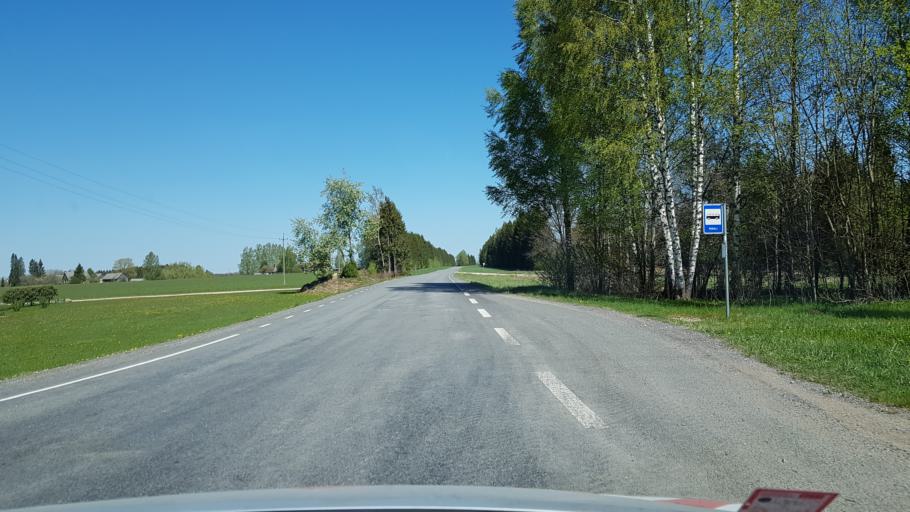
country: EE
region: Vorumaa
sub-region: Voru linn
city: Voru
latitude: 57.9421
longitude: 26.9535
